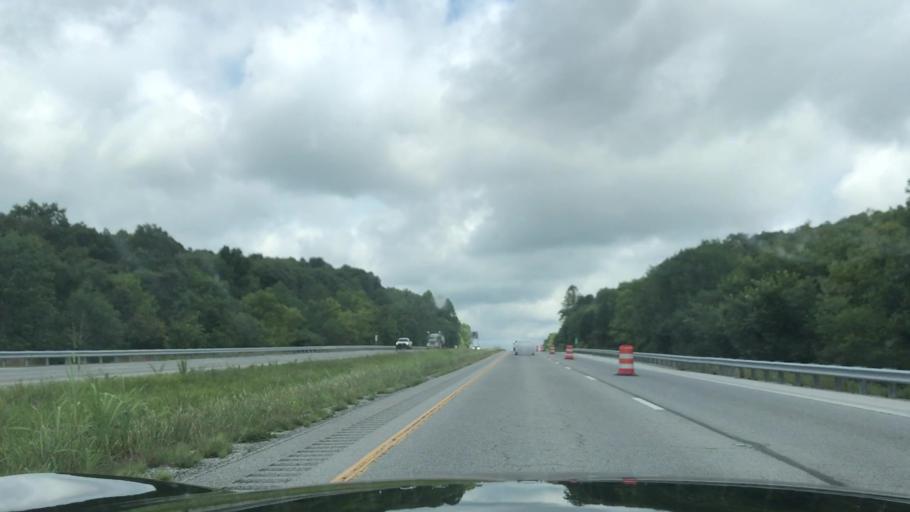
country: US
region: Kentucky
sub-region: Butler County
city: Morgantown
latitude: 37.0950
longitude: -86.6313
